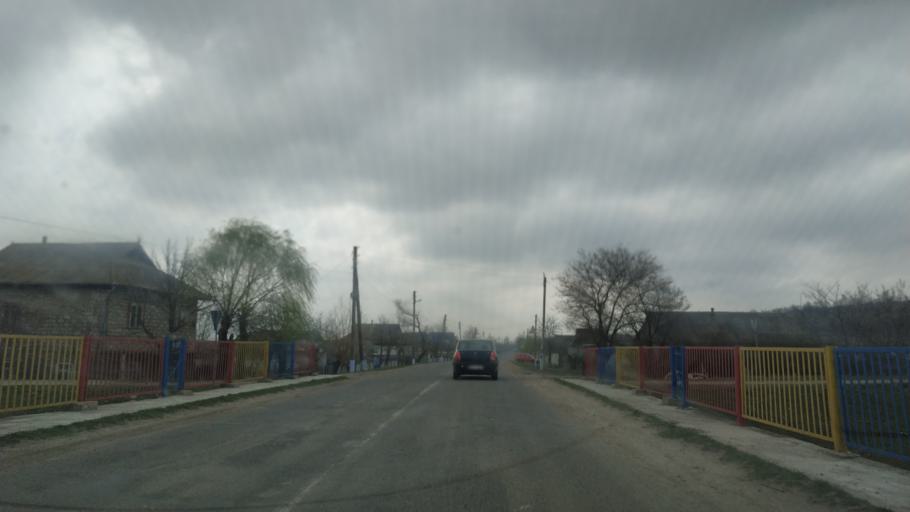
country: MD
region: Basarabeasca
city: Basarabeasca
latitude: 46.3772
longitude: 28.9213
